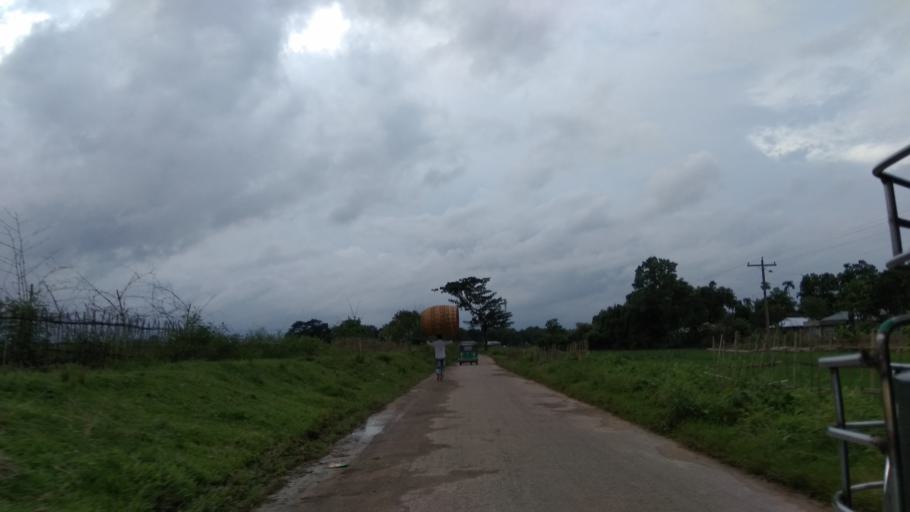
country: IN
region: Tripura
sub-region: Dhalai
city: Kamalpur
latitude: 24.2107
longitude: 91.8603
